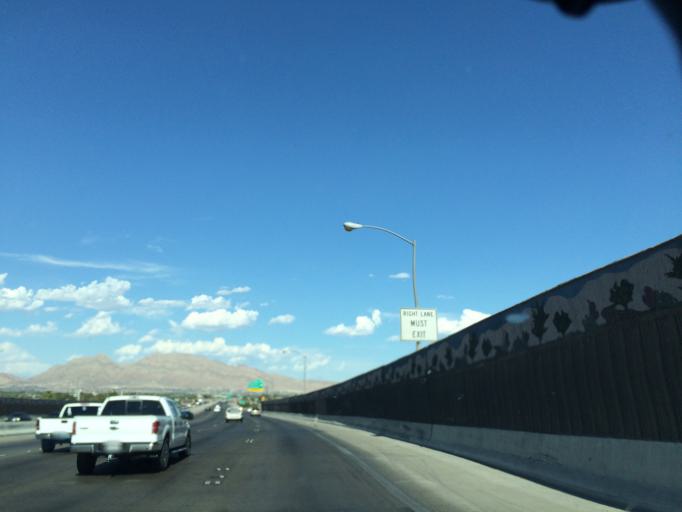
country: US
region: Nevada
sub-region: Clark County
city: Las Vegas
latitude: 36.1678
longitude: -115.1239
